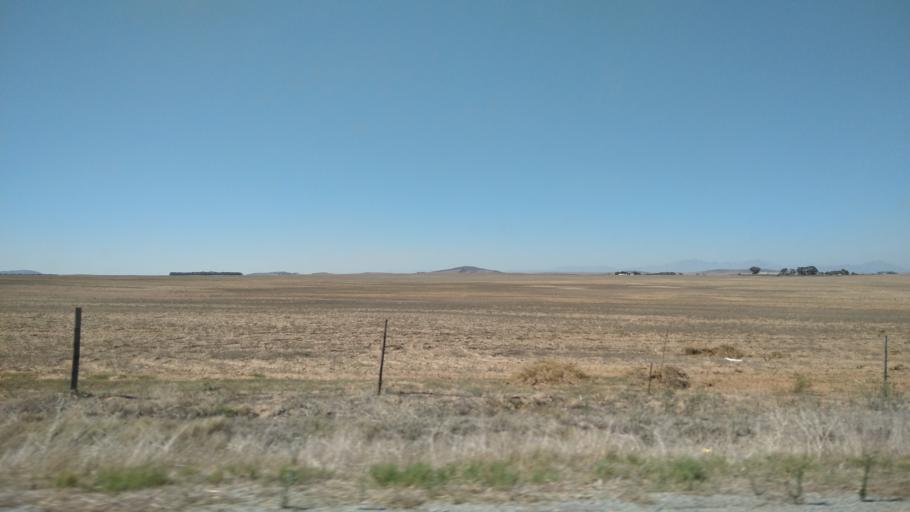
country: ZA
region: Western Cape
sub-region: West Coast District Municipality
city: Moorreesburg
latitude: -33.2399
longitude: 18.5700
